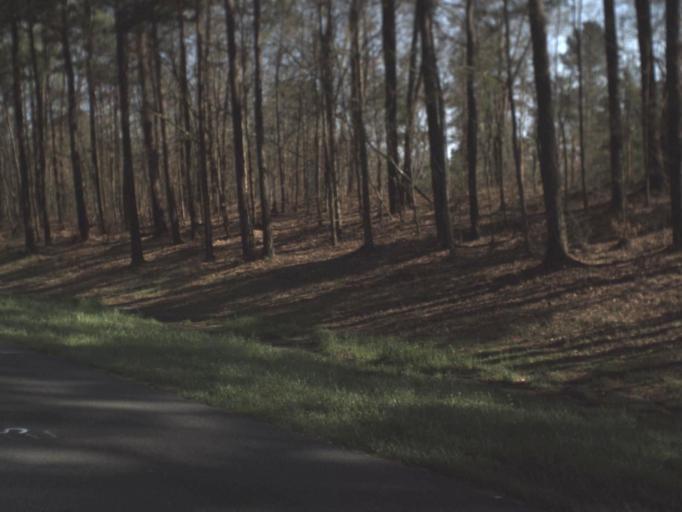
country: US
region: Florida
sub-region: Gadsden County
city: Midway
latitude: 30.5280
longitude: -84.5050
